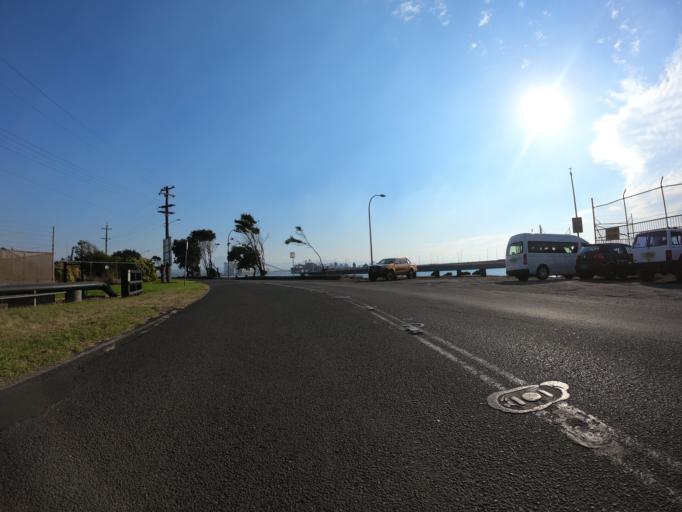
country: AU
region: New South Wales
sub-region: Wollongong
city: Cringila
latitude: -34.4650
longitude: 150.8997
